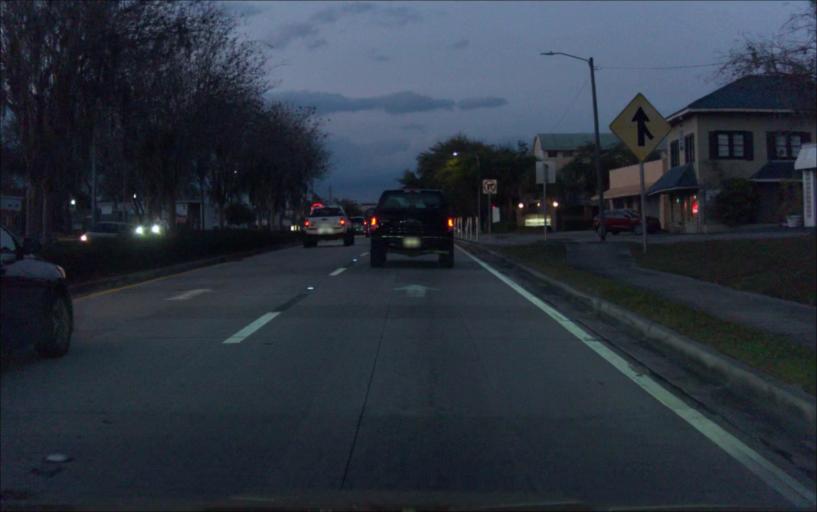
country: US
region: Florida
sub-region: Orange County
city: Maitland
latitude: 28.6181
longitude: -81.3644
